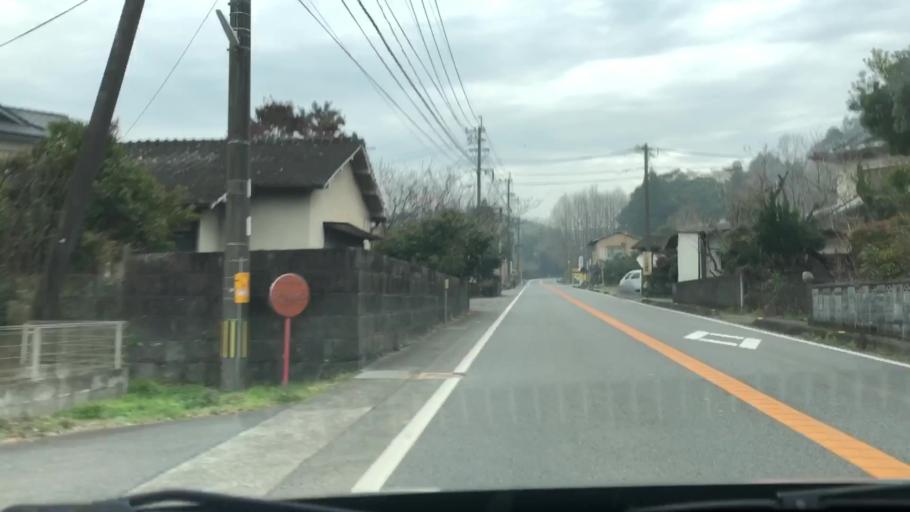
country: JP
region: Oita
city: Usuki
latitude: 33.0316
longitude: 131.6913
